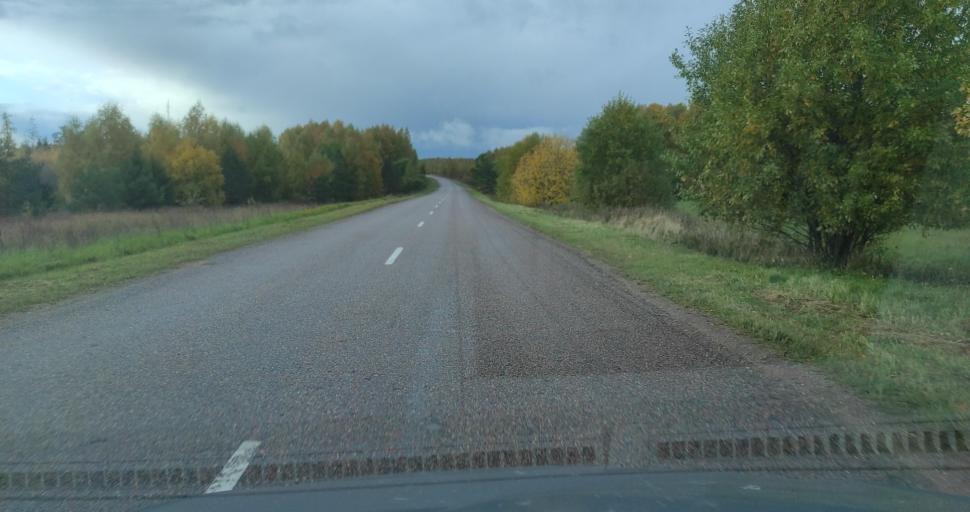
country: LV
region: Vainode
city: Vainode
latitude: 56.5856
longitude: 21.8954
